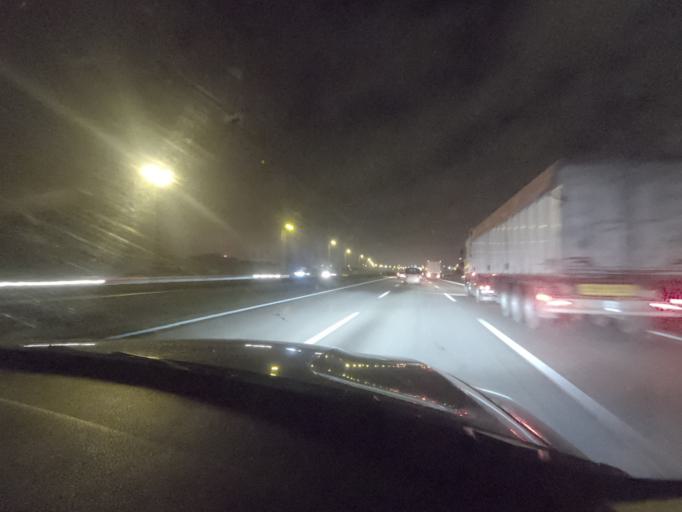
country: PT
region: Lisbon
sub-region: Alenquer
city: Carregado
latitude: 39.0311
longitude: -8.9609
